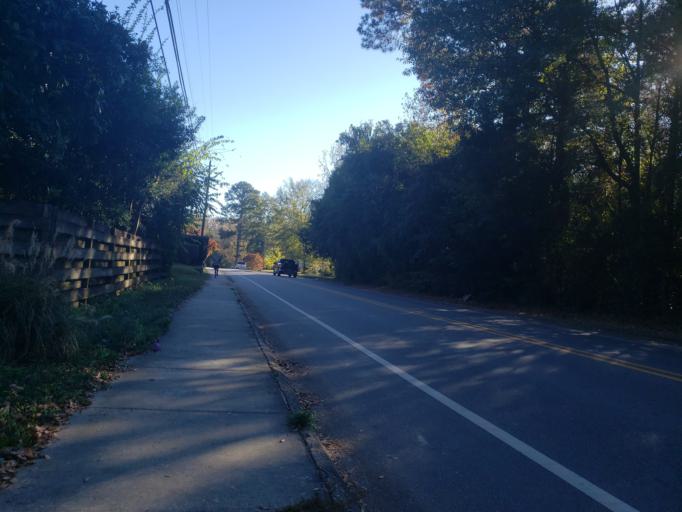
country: US
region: Alabama
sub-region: Lee County
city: Auburn
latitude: 32.5924
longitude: -85.4800
